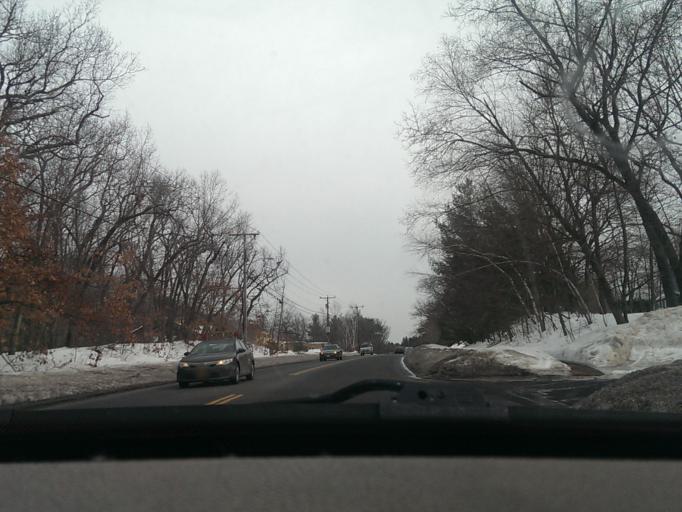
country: US
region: Massachusetts
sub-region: Hampden County
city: East Longmeadow
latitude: 42.0600
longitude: -72.5431
